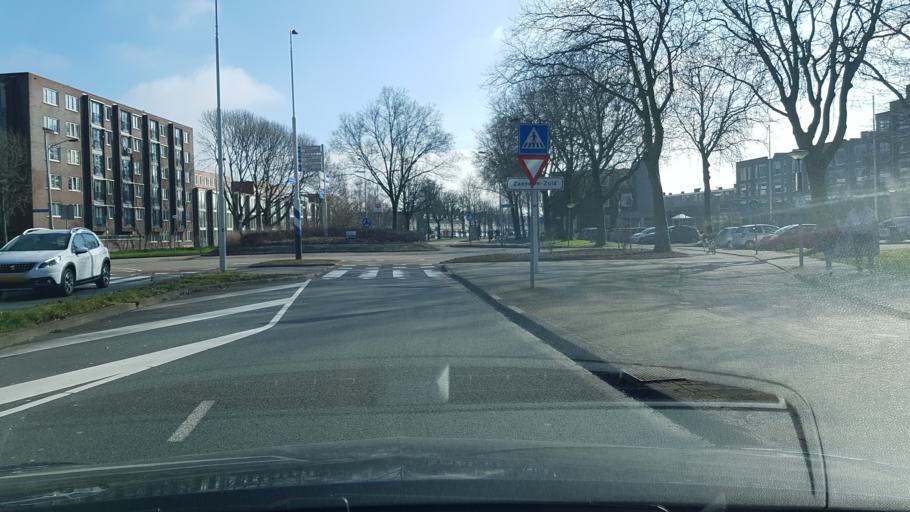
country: NL
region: North Holland
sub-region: Gemeente Zaanstad
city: Zaandam
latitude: 52.4420
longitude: 4.8320
